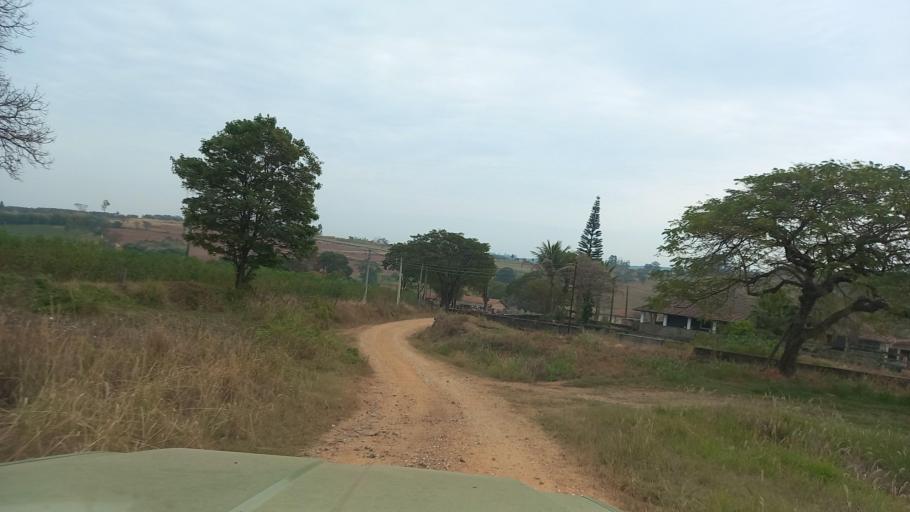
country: BR
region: Sao Paulo
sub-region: Moji-Guacu
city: Mogi-Gaucu
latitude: -22.2743
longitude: -46.8347
